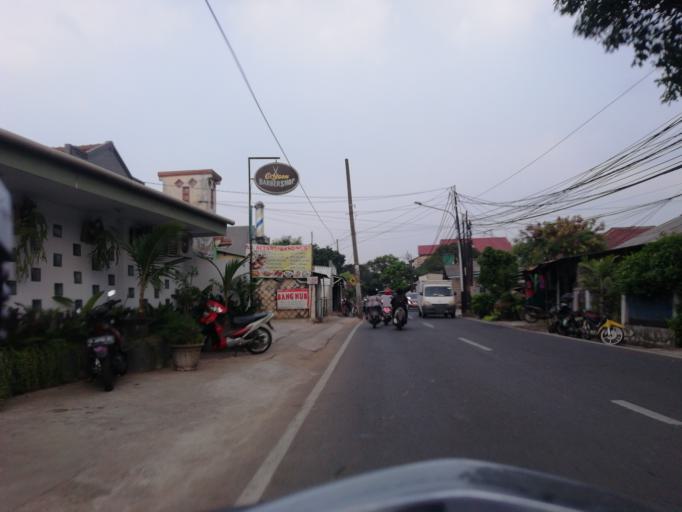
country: ID
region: West Java
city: Depok
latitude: -6.3358
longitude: 106.8290
